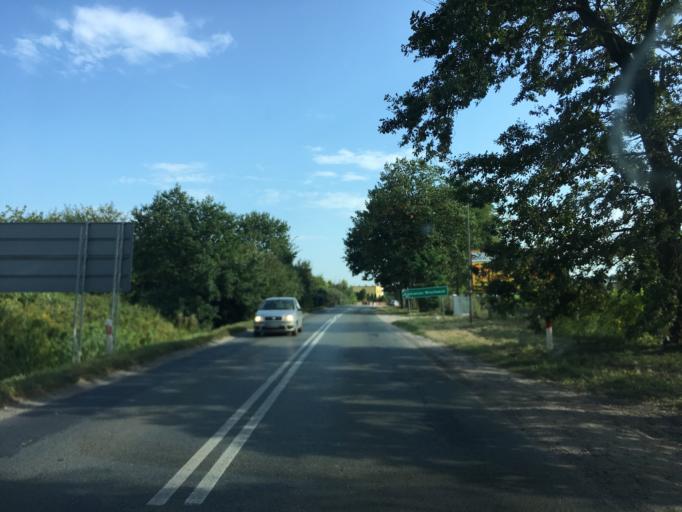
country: PL
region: Lower Silesian Voivodeship
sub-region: Powiat wroclawski
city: Kamieniec Wroclawski
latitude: 51.0862
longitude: 17.1680
